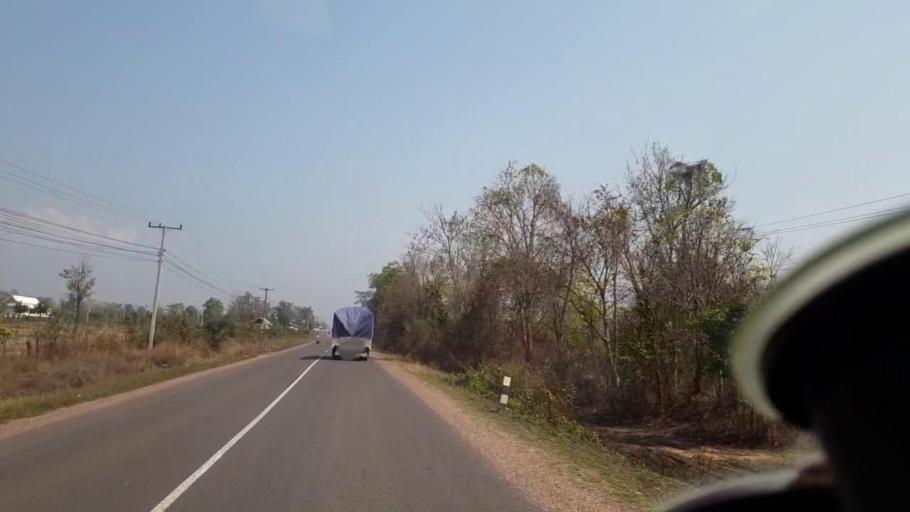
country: TH
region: Nong Khai
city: Phon Phisai
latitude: 18.0938
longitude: 103.0150
